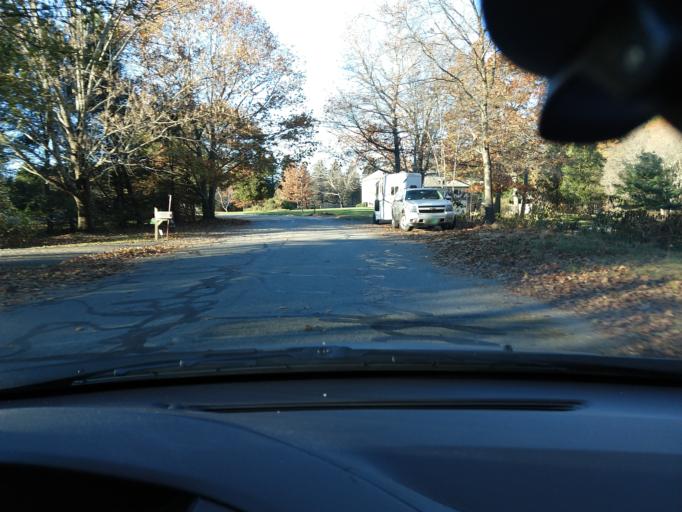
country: US
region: Massachusetts
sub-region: Middlesex County
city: Carlisle
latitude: 42.4998
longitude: -71.3222
